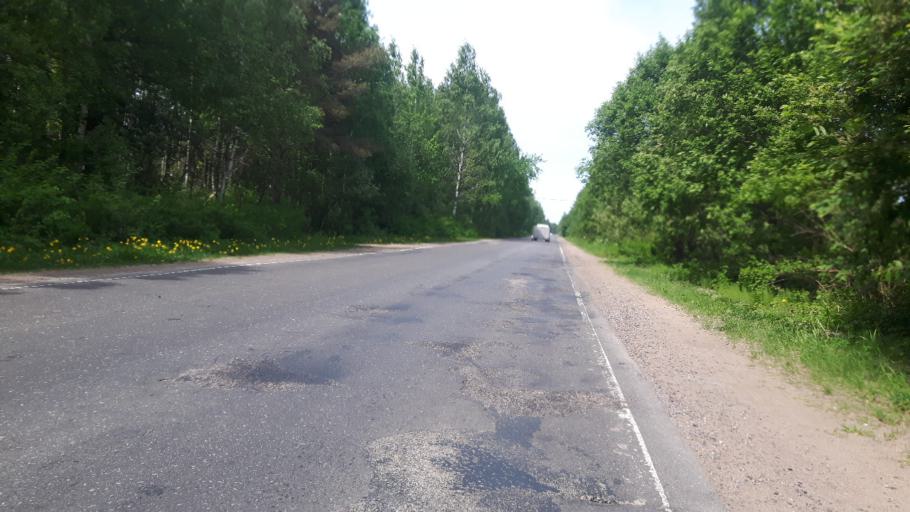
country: RU
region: Leningrad
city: Ust'-Luga
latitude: 59.6408
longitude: 28.2768
